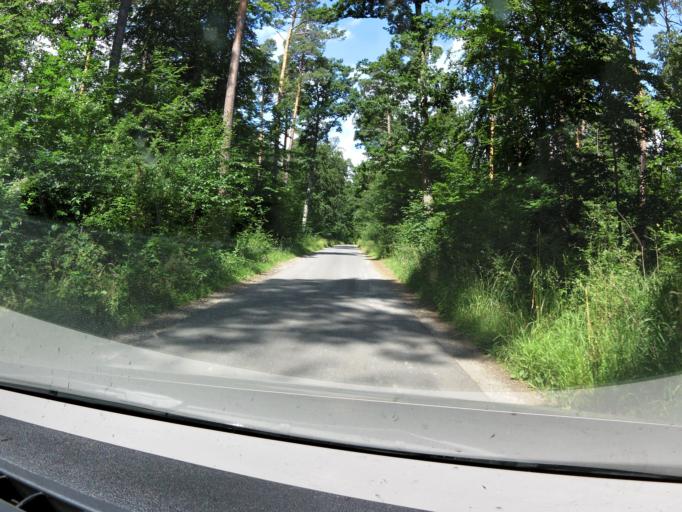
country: DE
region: Baden-Wuerttemberg
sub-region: Tuebingen Region
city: Tuebingen
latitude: 48.5516
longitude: 8.9991
